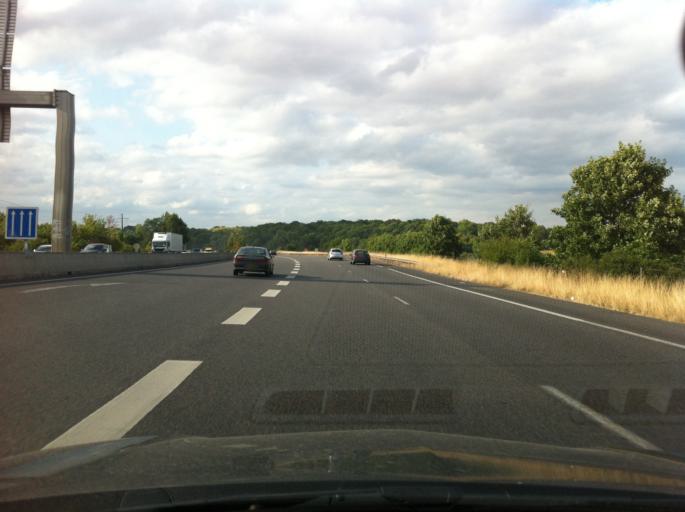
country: FR
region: Ile-de-France
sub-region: Departement de Seine-et-Marne
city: Brie-Comte-Robert
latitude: 48.6612
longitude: 2.6134
